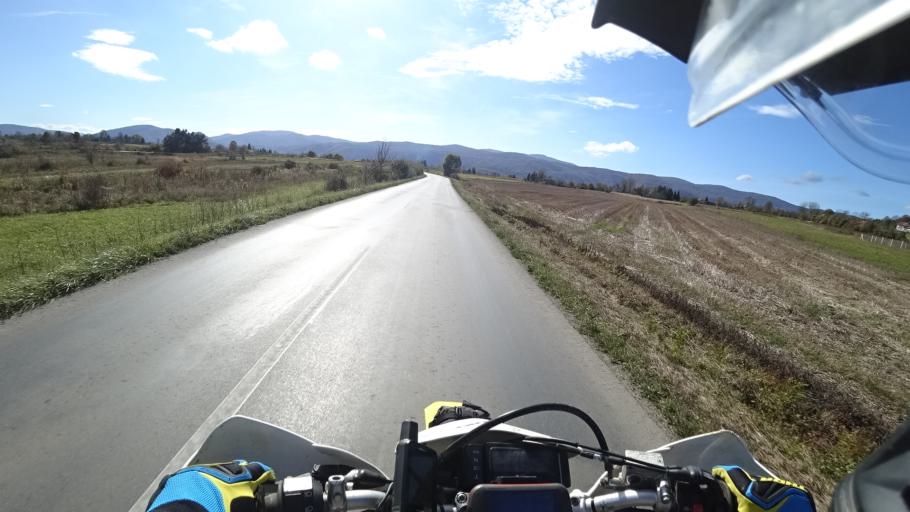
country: HR
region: Karlovacka
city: Plaski
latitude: 45.1083
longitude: 15.3603
